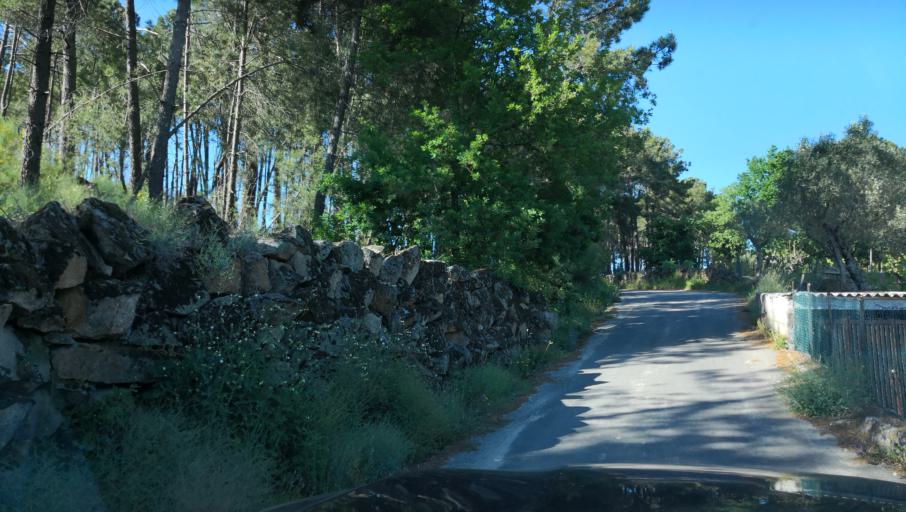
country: PT
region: Vila Real
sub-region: Vila Real
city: Vila Real
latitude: 41.3293
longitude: -7.7343
